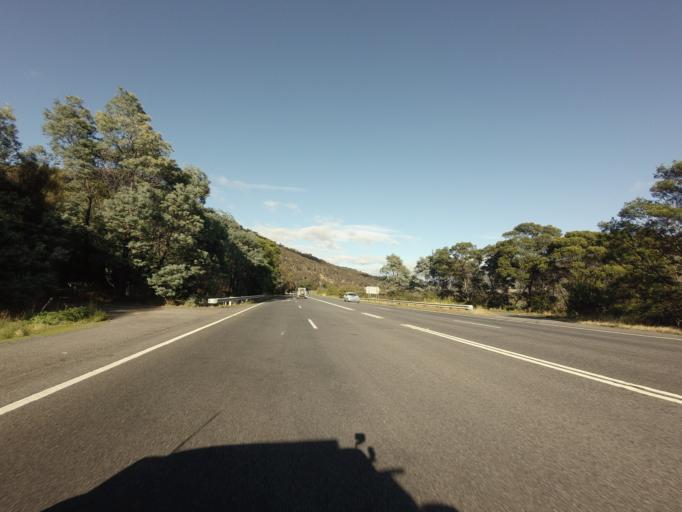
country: AU
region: Tasmania
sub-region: Glenorchy
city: Granton
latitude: -42.7544
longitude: 147.1624
